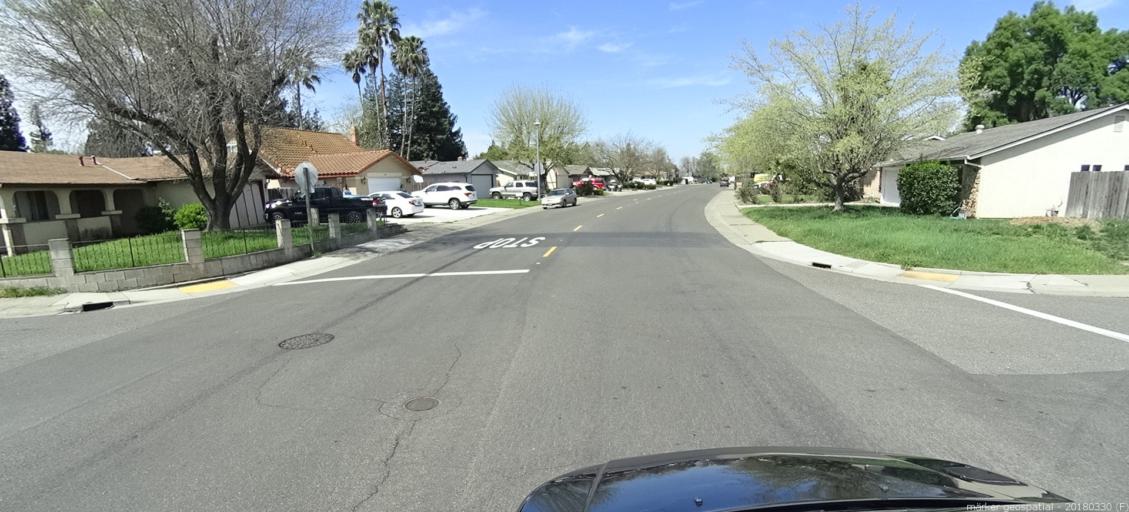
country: US
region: California
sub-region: Sacramento County
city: Rosemont
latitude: 38.5413
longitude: -121.3687
